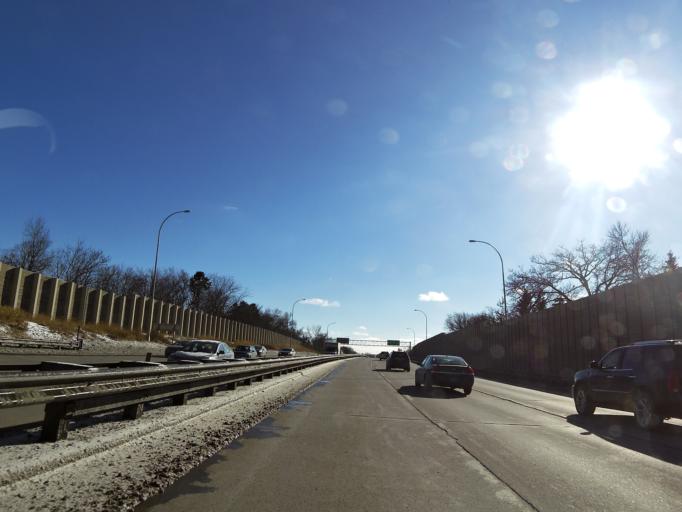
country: US
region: Minnesota
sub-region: Hennepin County
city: Saint Louis Park
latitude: 44.9211
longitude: -93.3495
